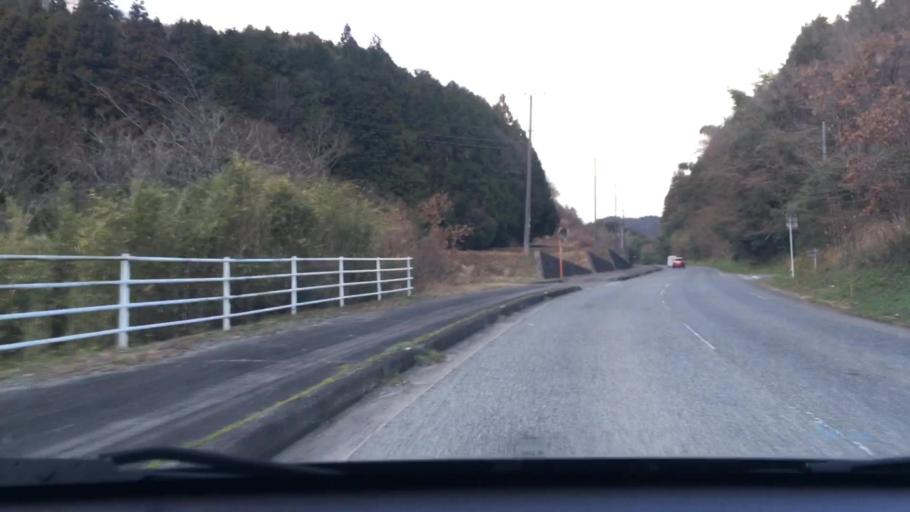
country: JP
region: Oita
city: Bungo-Takada-shi
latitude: 33.4738
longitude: 131.3842
